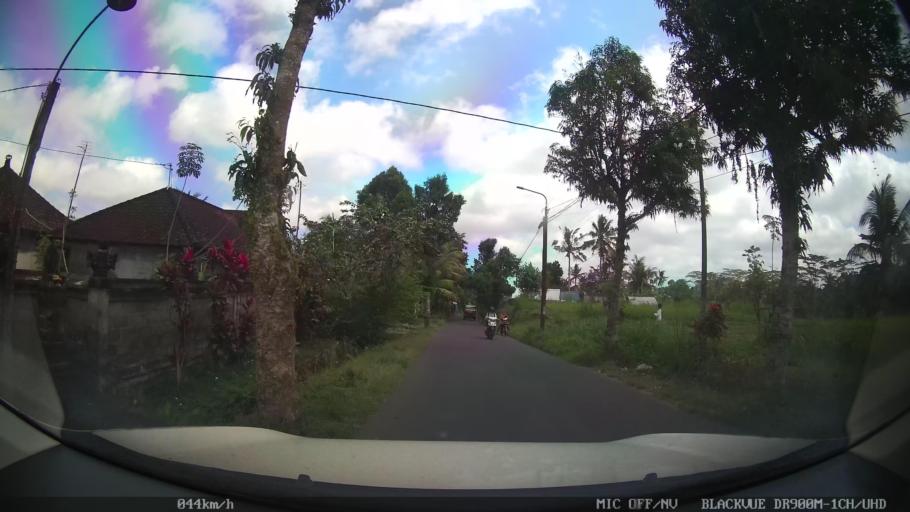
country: ID
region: Bali
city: Banjar Madangan Kaja
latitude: -8.4872
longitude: 115.3211
